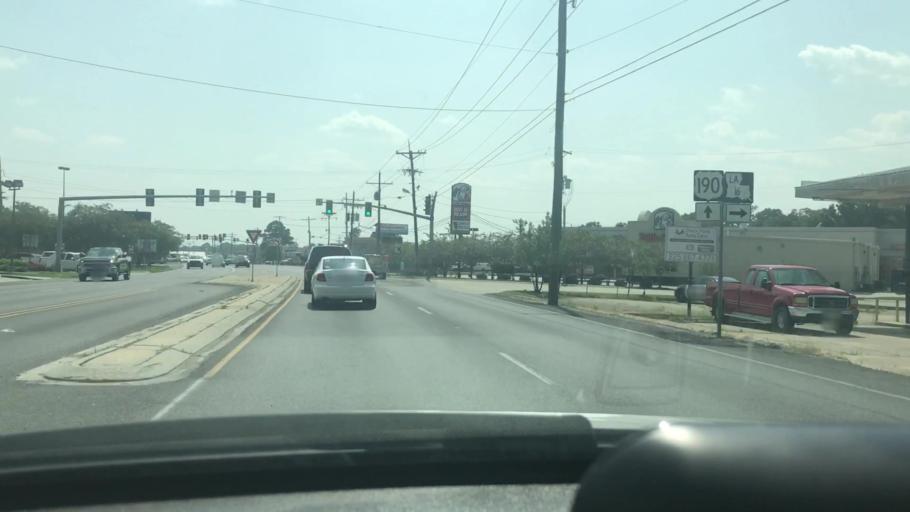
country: US
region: Louisiana
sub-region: Livingston Parish
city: Denham Springs
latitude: 30.4828
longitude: -90.9546
